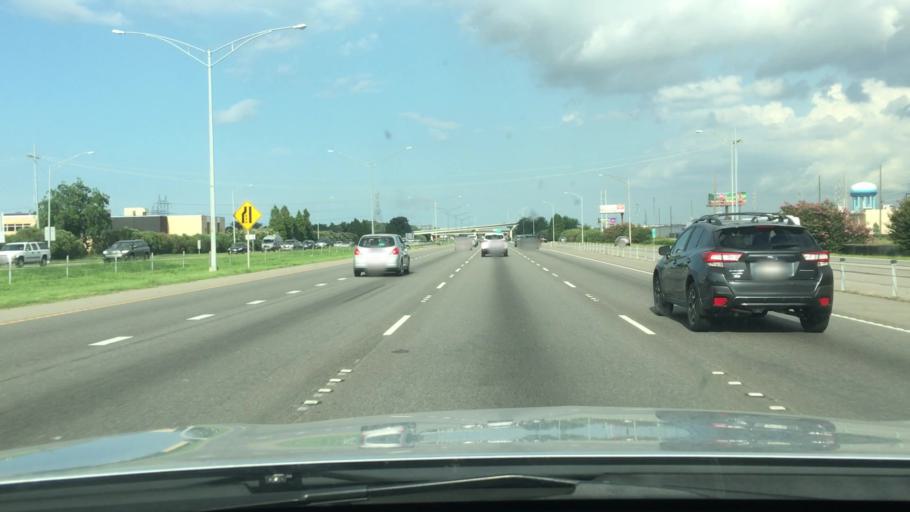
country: US
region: Louisiana
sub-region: Jefferson Parish
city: Kenner
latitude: 30.0085
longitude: -90.2300
